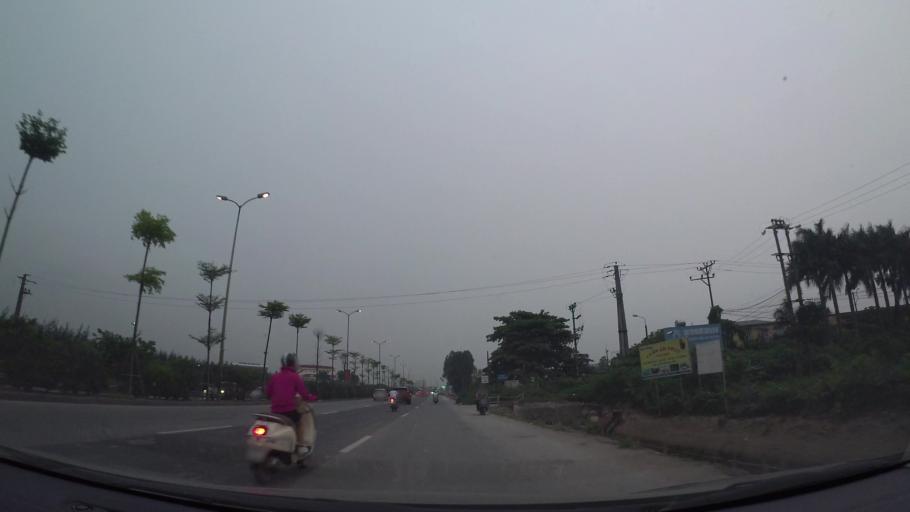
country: VN
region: Ha Noi
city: Hoan Kiem
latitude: 21.0456
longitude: 105.8948
